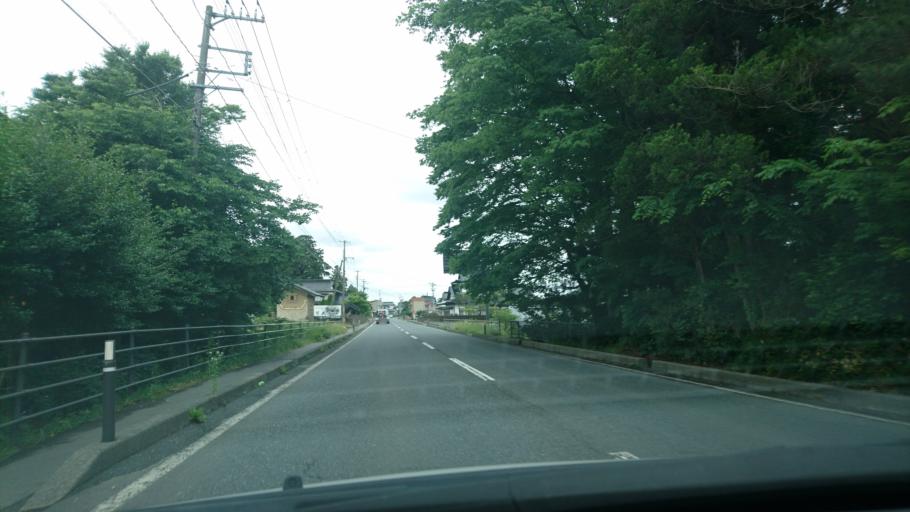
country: JP
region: Iwate
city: Ichinoseki
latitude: 38.9756
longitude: 141.1171
